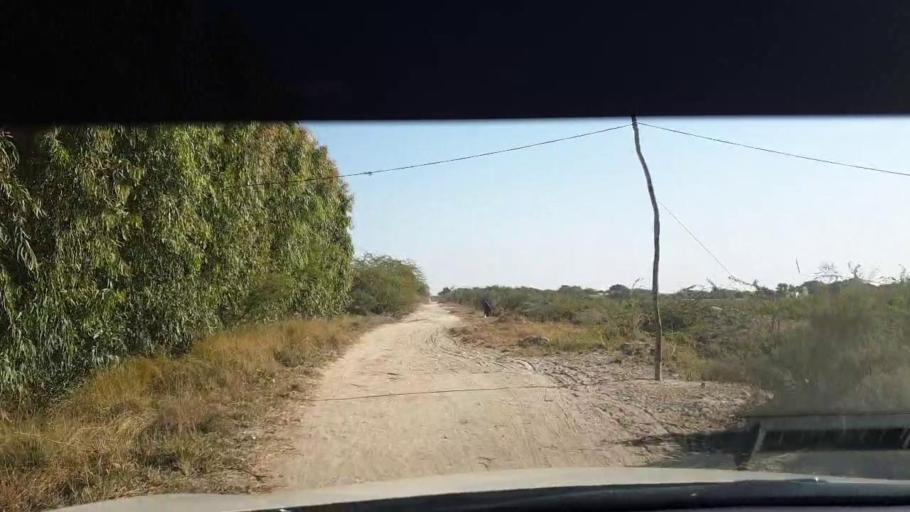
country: PK
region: Sindh
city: Berani
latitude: 25.8092
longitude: 68.9371
